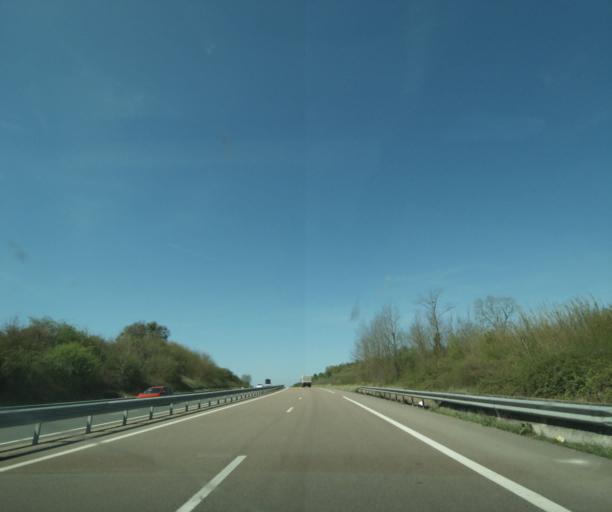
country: FR
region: Bourgogne
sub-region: Departement de la Nievre
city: Pougues-les-Eaux
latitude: 47.0818
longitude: 3.1200
